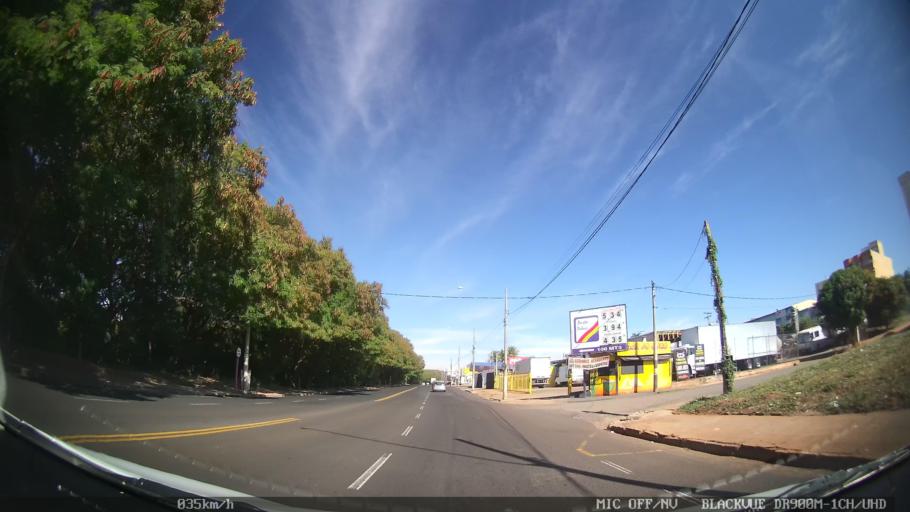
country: BR
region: Sao Paulo
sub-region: Sao Jose Do Rio Preto
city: Sao Jose do Rio Preto
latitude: -20.7988
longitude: -49.4022
